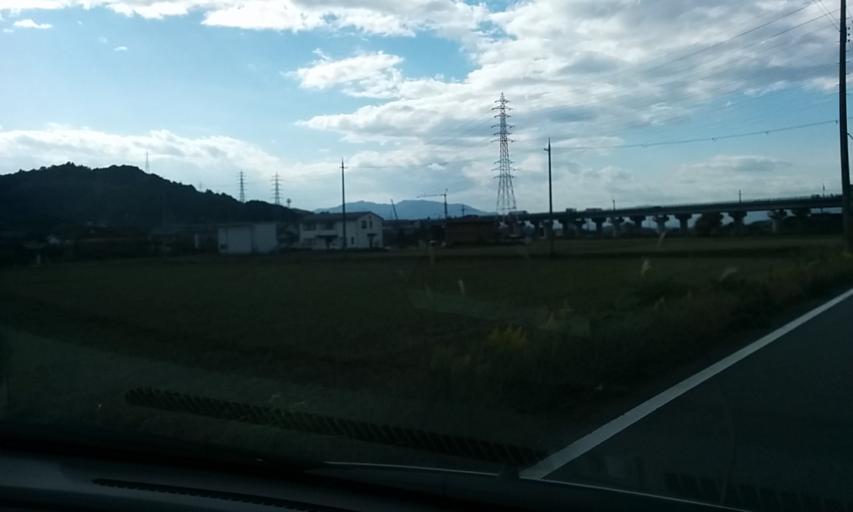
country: JP
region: Kyoto
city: Ayabe
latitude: 35.3065
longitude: 135.1953
